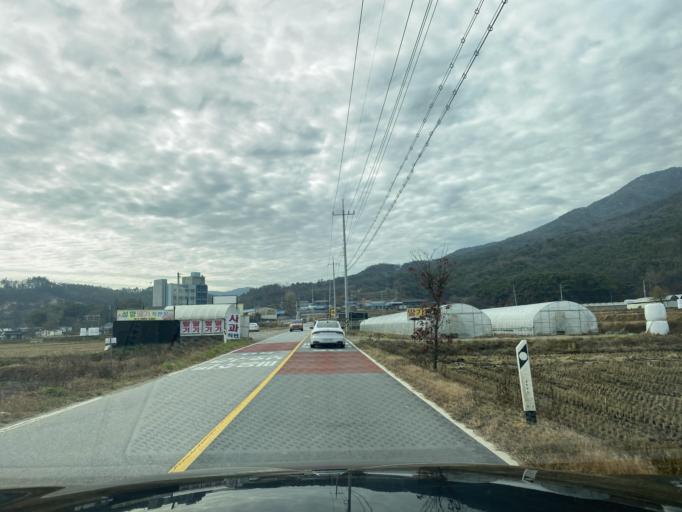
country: KR
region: Chungcheongnam-do
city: Hongsung
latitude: 36.6771
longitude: 126.6438
